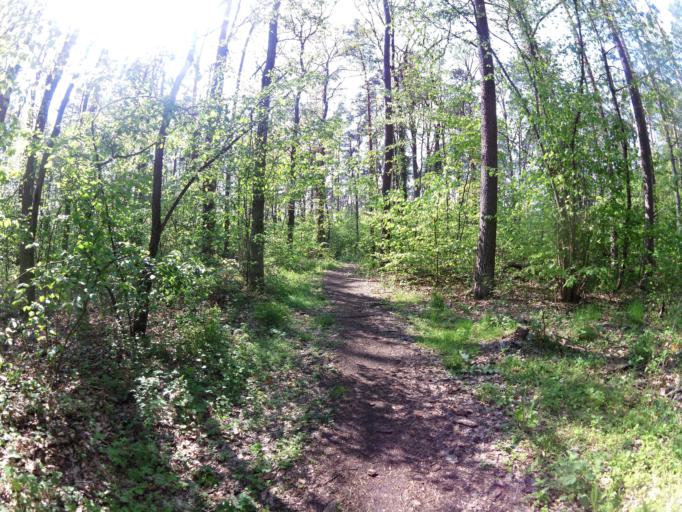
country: DE
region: Bavaria
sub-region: Regierungsbezirk Unterfranken
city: Sommerhausen
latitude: 49.7026
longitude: 10.0426
